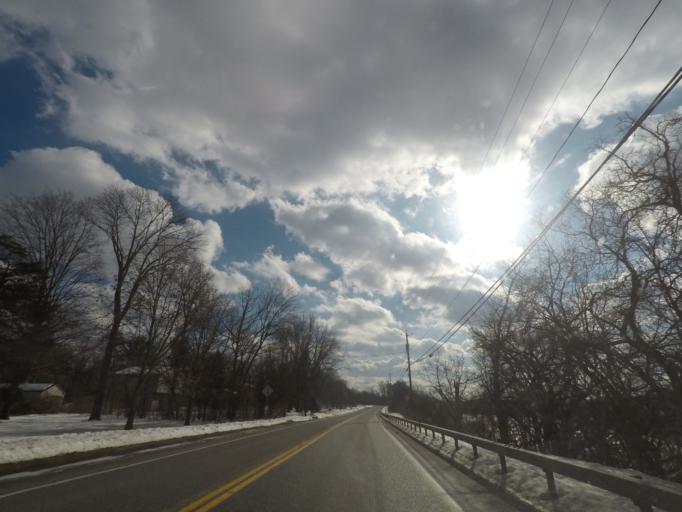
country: US
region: New York
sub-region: Schenectady County
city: East Glenville
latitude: 42.8496
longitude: -73.8783
